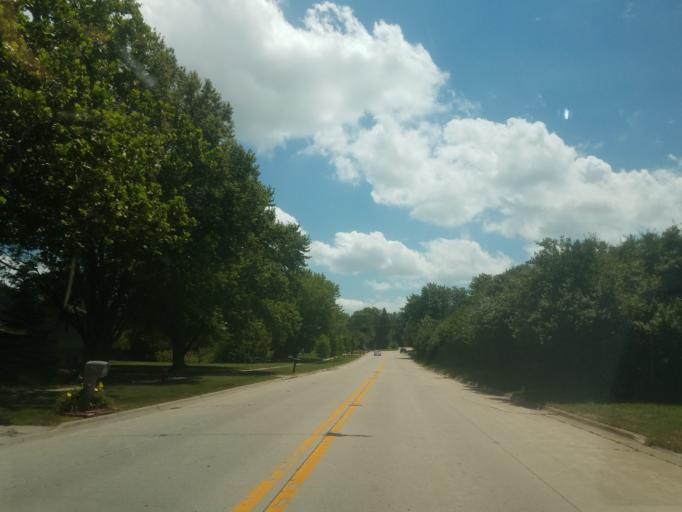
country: US
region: Illinois
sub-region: McLean County
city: Normal
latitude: 40.5044
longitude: -89.0209
